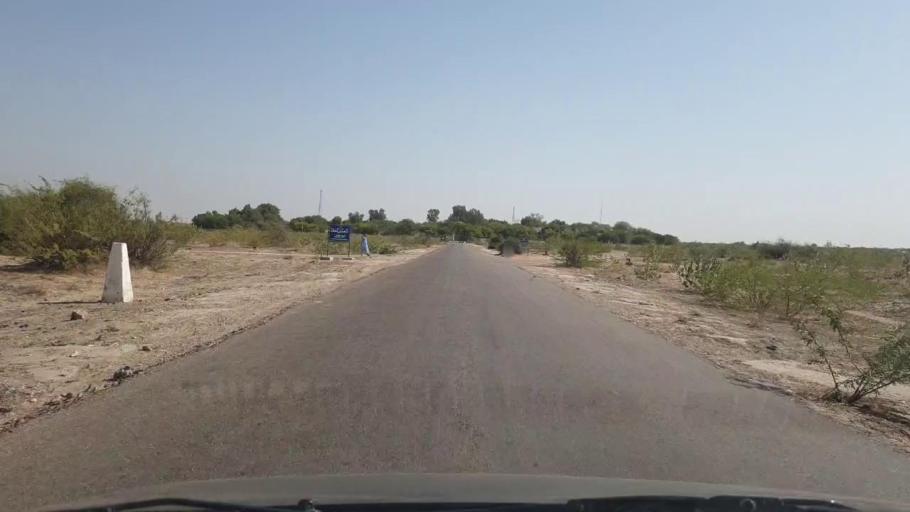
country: PK
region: Sindh
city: Chor
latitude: 25.5225
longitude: 69.8243
